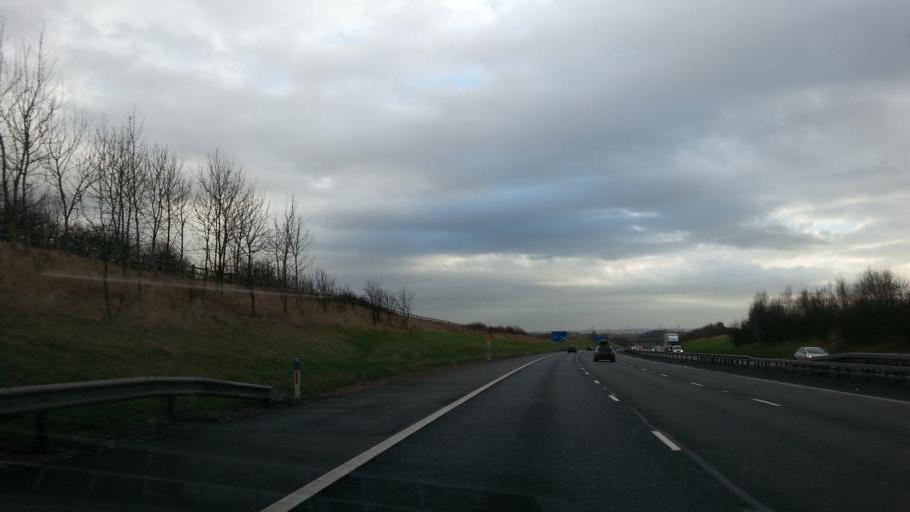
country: GB
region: England
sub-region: Warwickshire
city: Curdworth
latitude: 52.5625
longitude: -1.7560
